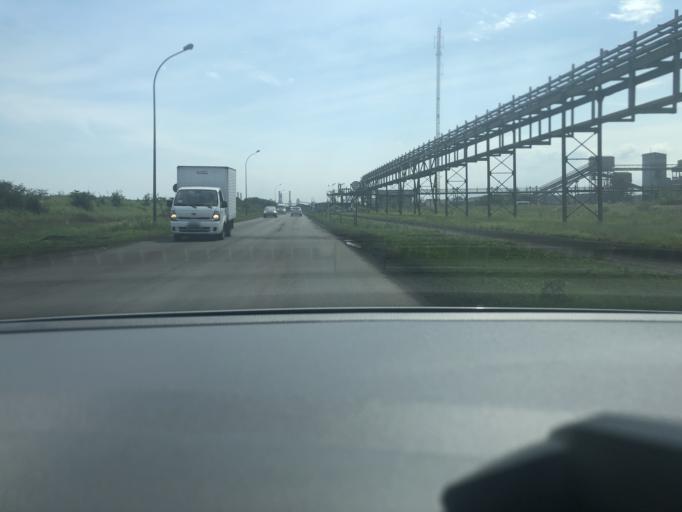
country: BR
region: Rio de Janeiro
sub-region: Itaguai
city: Itaguai
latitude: -22.9150
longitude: -43.7398
